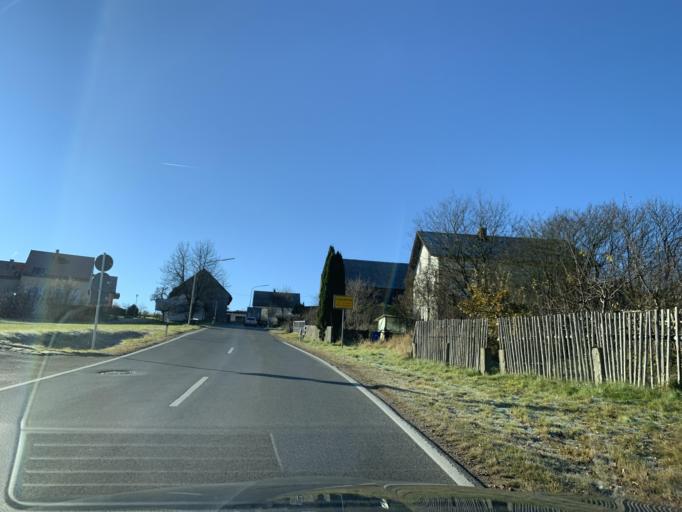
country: DE
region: Bavaria
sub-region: Upper Palatinate
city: Oberviechtach
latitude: 49.4471
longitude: 12.4189
